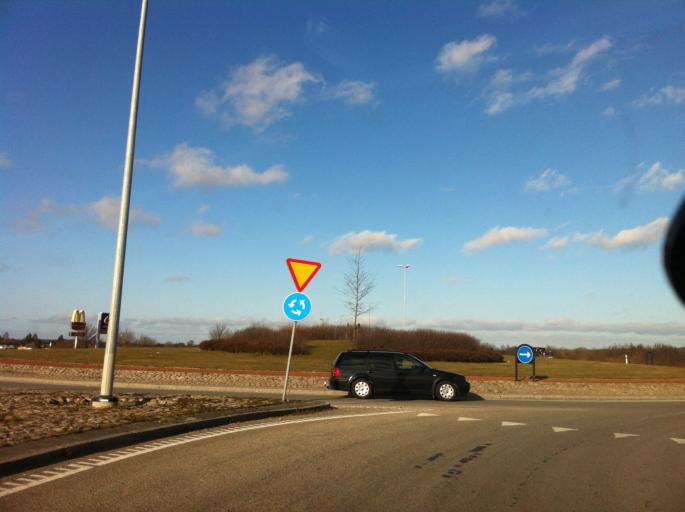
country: SE
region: Skane
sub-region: Svedala Kommun
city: Svedala
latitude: 55.5147
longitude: 13.2487
